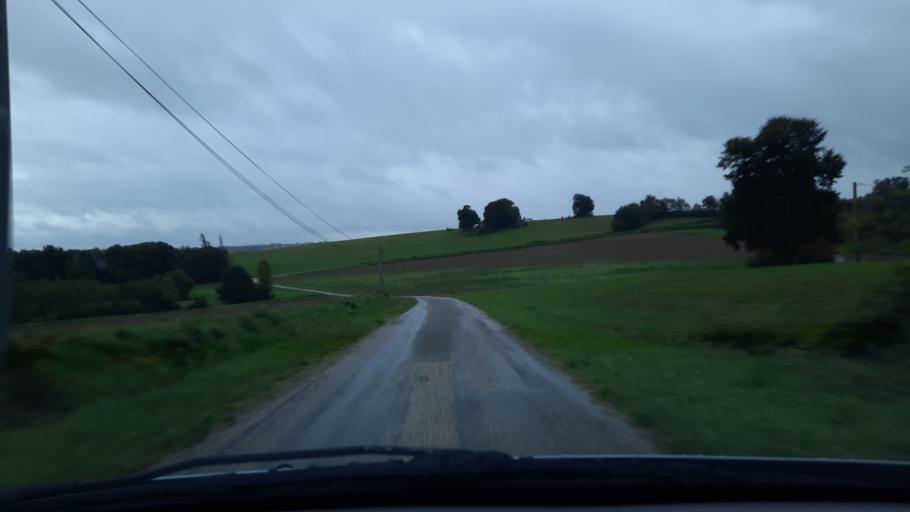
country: FR
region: Midi-Pyrenees
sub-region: Departement du Tarn-et-Garonne
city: Molieres
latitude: 44.1936
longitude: 1.3112
